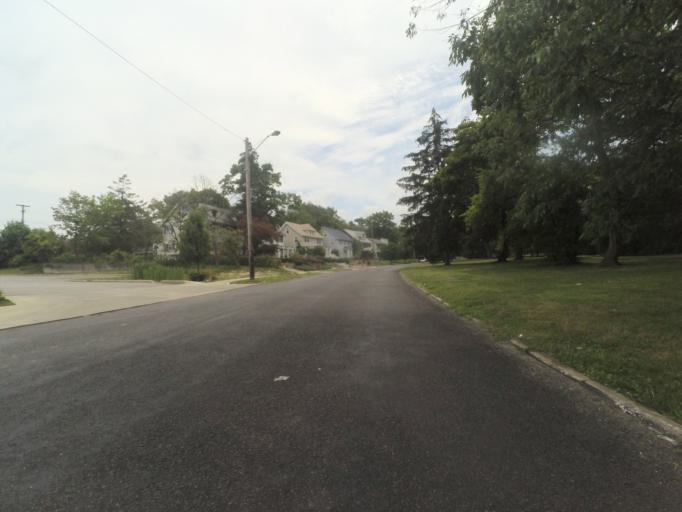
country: US
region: Ohio
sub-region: Cuyahoga County
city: Cleveland Heights
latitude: 41.5149
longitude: -81.5704
